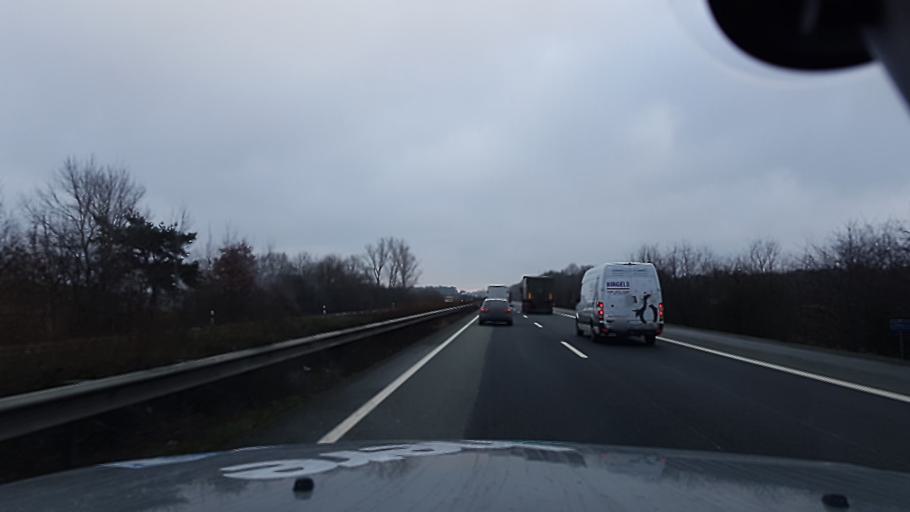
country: DE
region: Lower Saxony
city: Rieste
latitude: 52.4599
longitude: 8.0462
